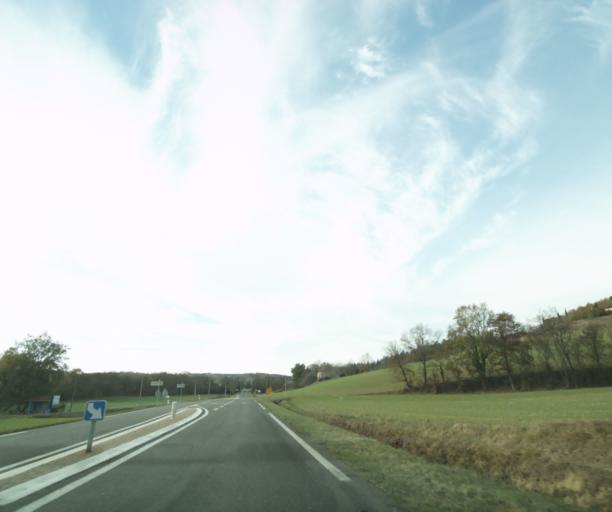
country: FR
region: Midi-Pyrenees
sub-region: Departement du Gers
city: Jegun
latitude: 43.6930
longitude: 0.4659
